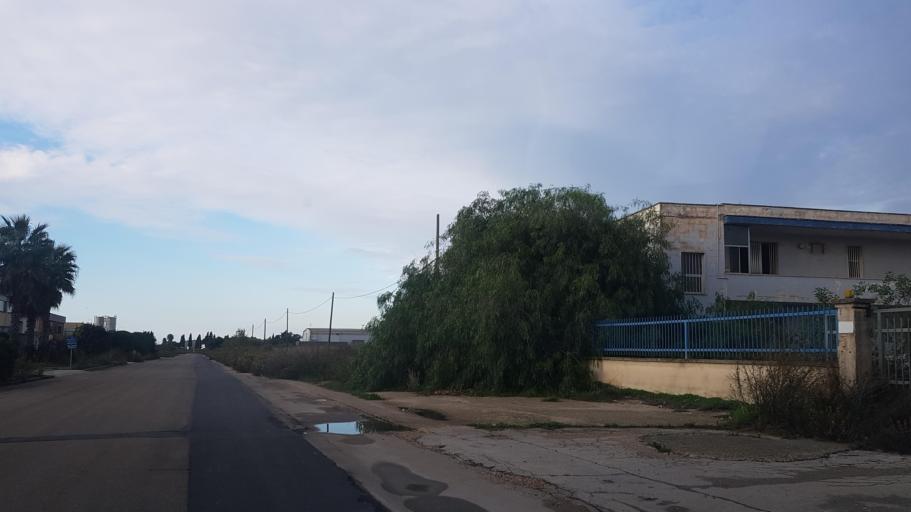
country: IT
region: Apulia
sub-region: Provincia di Brindisi
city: Materdomini
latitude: 40.6290
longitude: 17.9715
